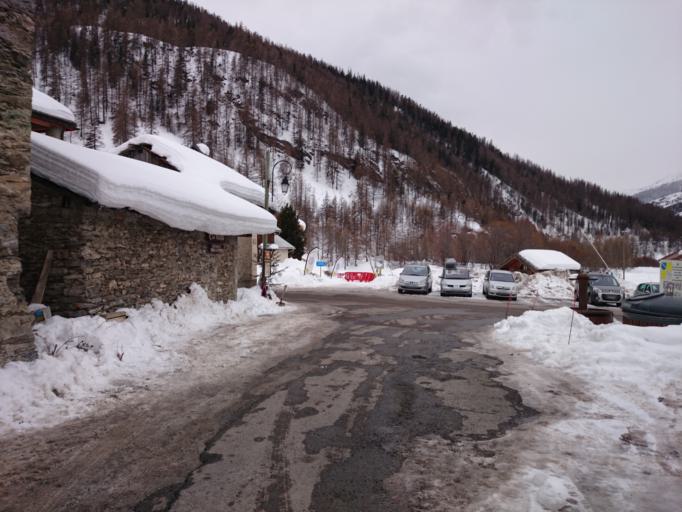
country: IT
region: Piedmont
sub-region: Provincia di Torino
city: Prali
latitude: 44.7926
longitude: 6.9282
